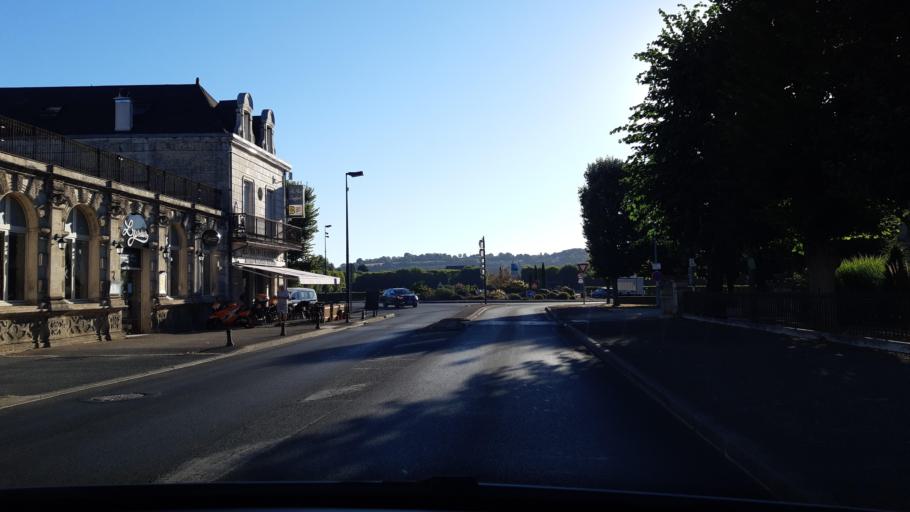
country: FR
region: Poitou-Charentes
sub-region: Departement des Deux-Sevres
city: Exireuil
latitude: 46.4145
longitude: -0.2019
